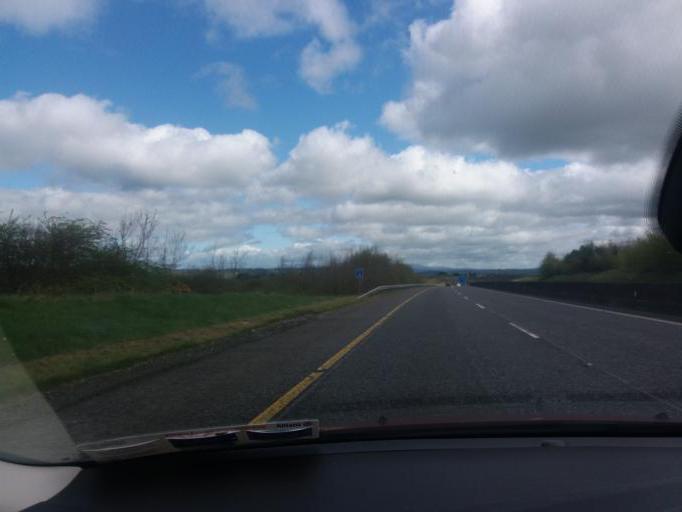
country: IE
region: Munster
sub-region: County Cork
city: Watergrasshill
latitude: 52.0416
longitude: -8.3148
